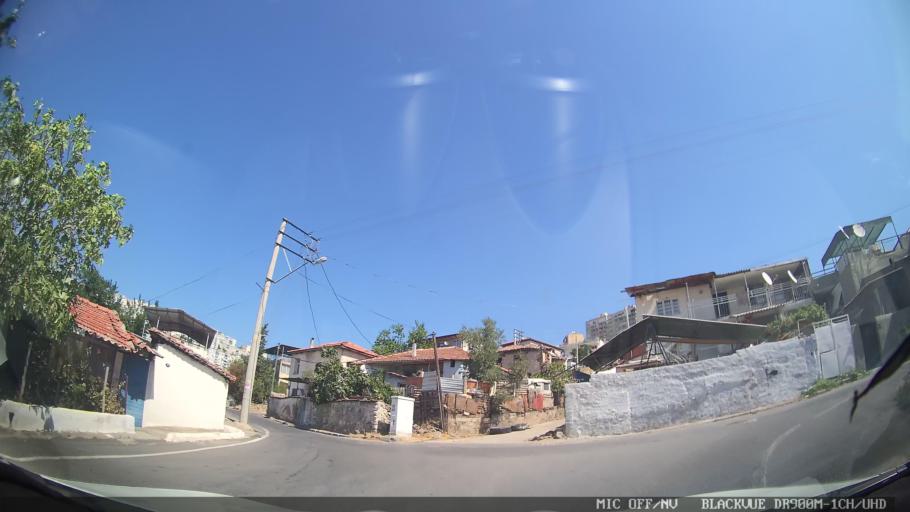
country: TR
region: Izmir
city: Karsiyaka
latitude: 38.5013
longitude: 27.0699
